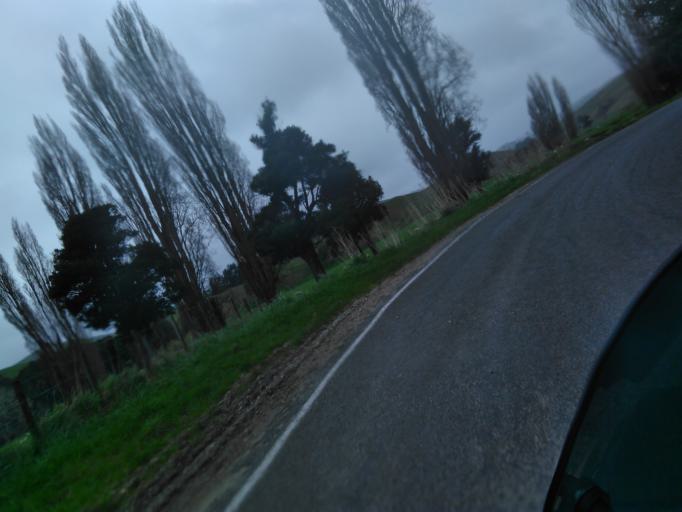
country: NZ
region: Gisborne
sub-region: Gisborne District
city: Gisborne
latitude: -38.6364
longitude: 177.6897
